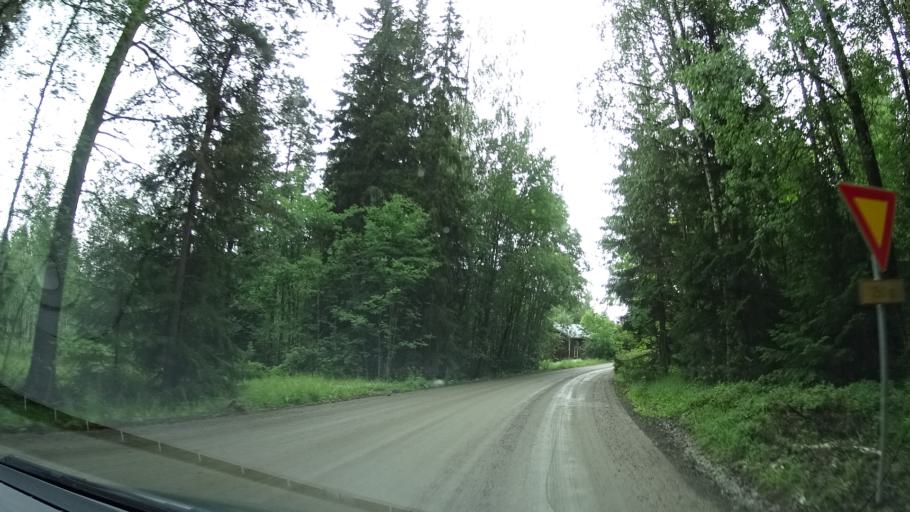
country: FI
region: Pirkanmaa
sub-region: Lounais-Pirkanmaa
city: Punkalaidun
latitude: 61.1038
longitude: 23.2793
